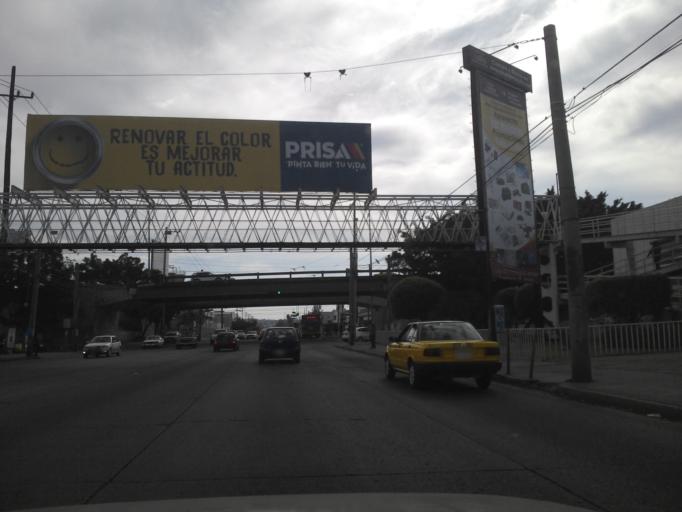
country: MX
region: Jalisco
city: Guadalajara
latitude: 20.6480
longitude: -103.3610
